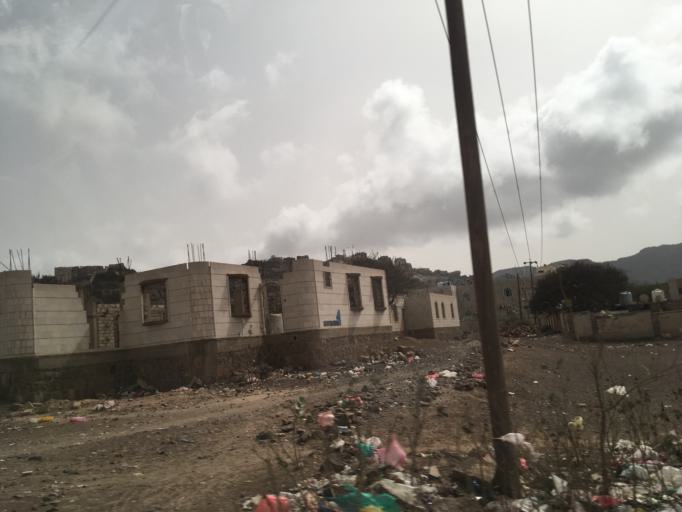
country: YE
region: Ad Dali'
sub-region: Ad Dhale'e
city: Dhalie
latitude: 13.7041
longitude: 44.7372
